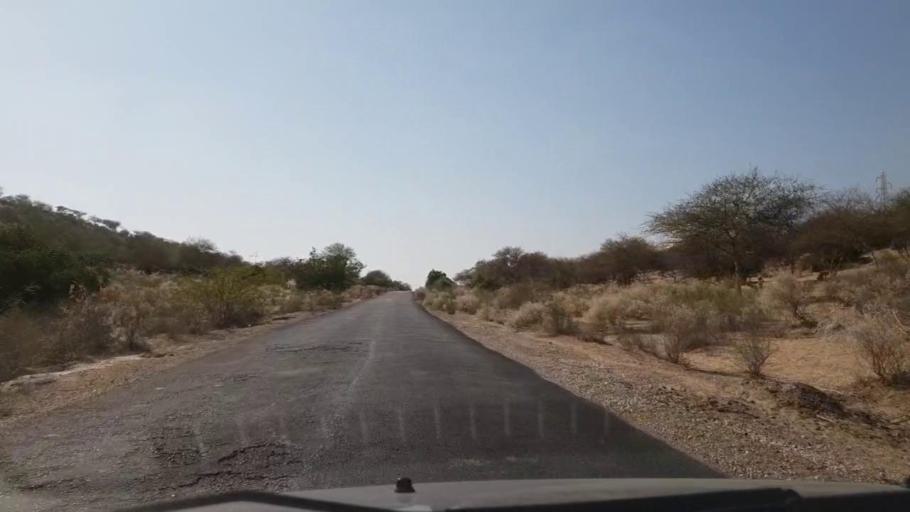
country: PK
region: Sindh
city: Mithi
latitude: 24.6757
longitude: 69.7737
